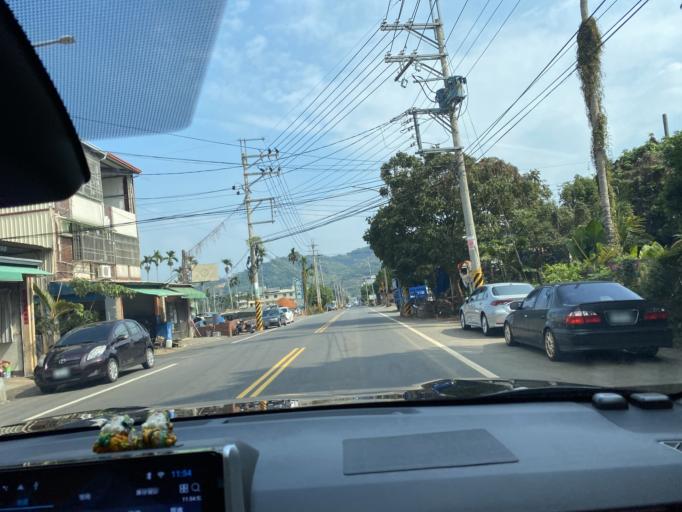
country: TW
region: Taiwan
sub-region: Nantou
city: Nantou
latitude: 23.8413
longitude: 120.6893
